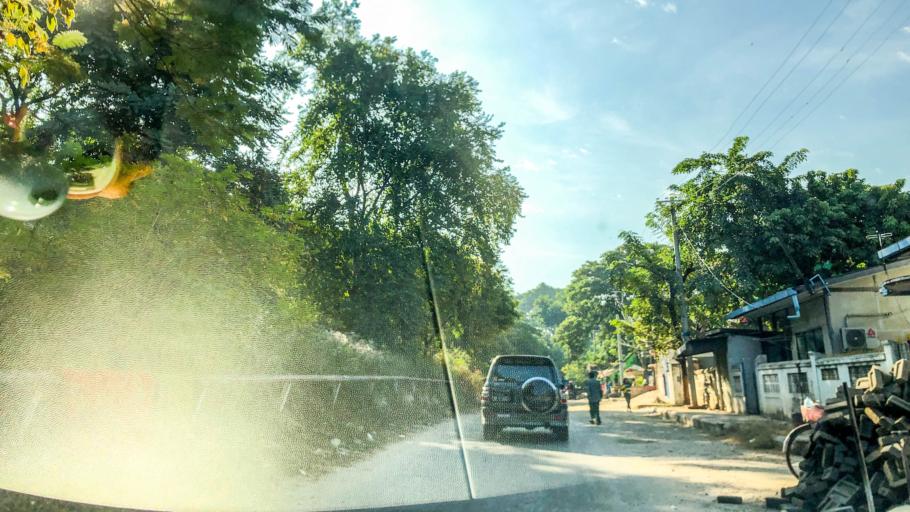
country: MM
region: Sagain
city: Sagaing
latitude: 21.8798
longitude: 95.9856
